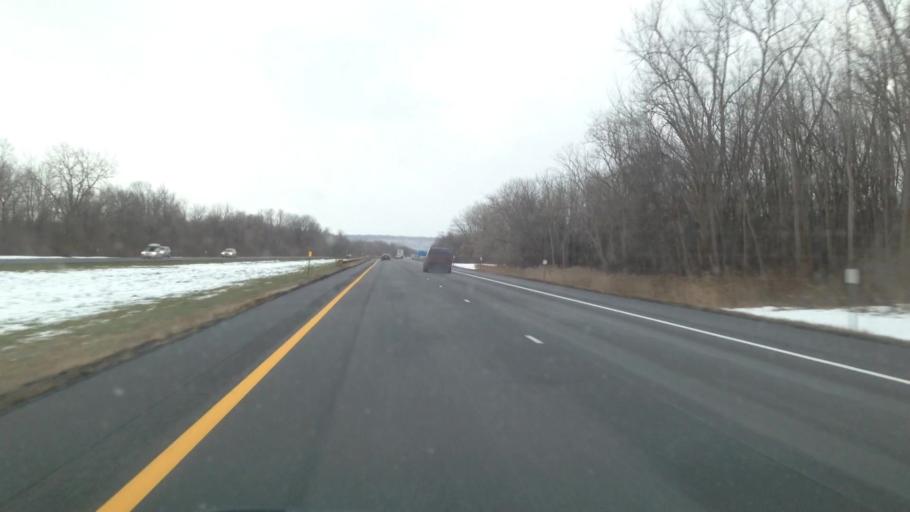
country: US
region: New York
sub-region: Montgomery County
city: Fonda
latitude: 42.9303
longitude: -74.4185
